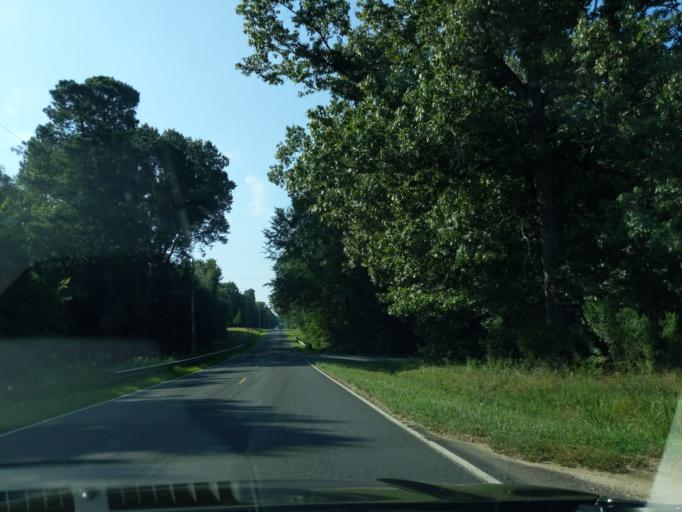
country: US
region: South Carolina
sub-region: Lexington County
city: Leesville
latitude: 34.0389
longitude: -81.5414
